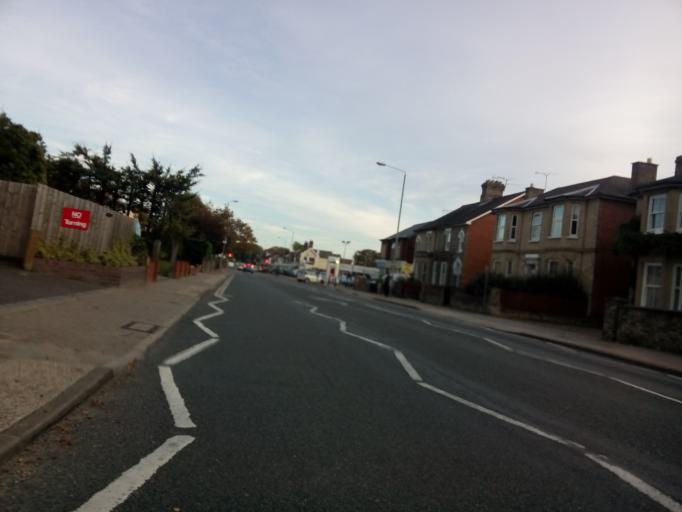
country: GB
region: England
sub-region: Suffolk
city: Ipswich
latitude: 52.0686
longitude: 1.1359
